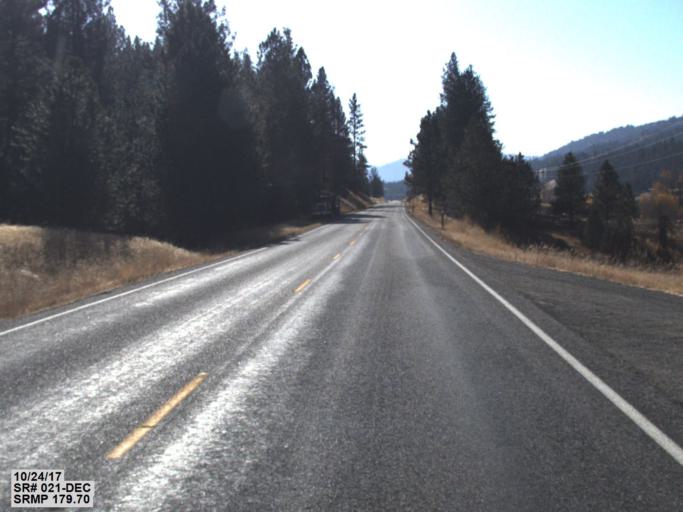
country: CA
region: British Columbia
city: Grand Forks
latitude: 48.8636
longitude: -118.6053
